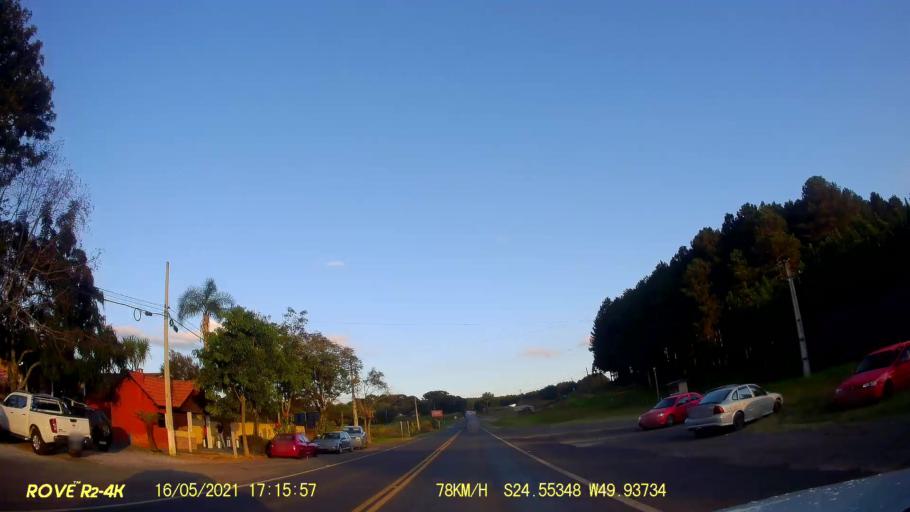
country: BR
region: Parana
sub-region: Pirai Do Sul
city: Pirai do Sul
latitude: -24.5537
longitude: -49.9372
